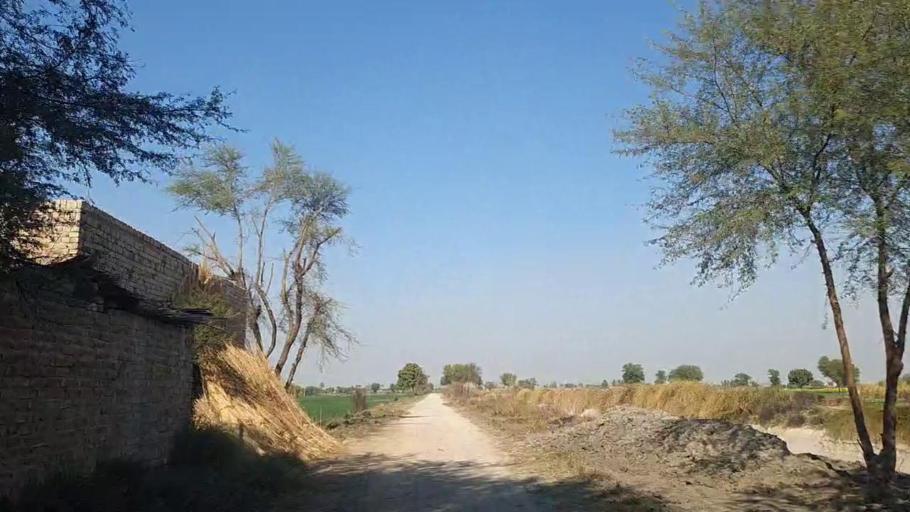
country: PK
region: Sindh
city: Sakrand
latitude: 26.2673
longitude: 68.2210
